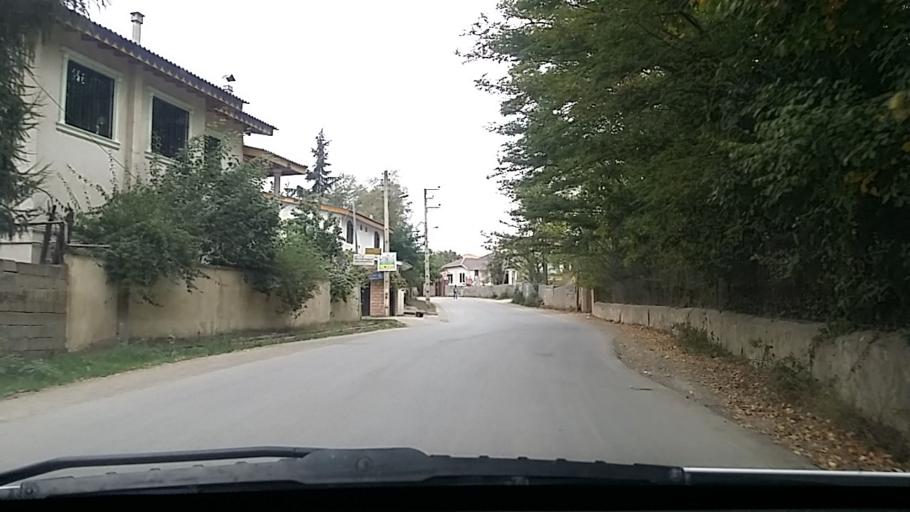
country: IR
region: Mazandaran
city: `Abbasabad
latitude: 36.5030
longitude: 51.1605
